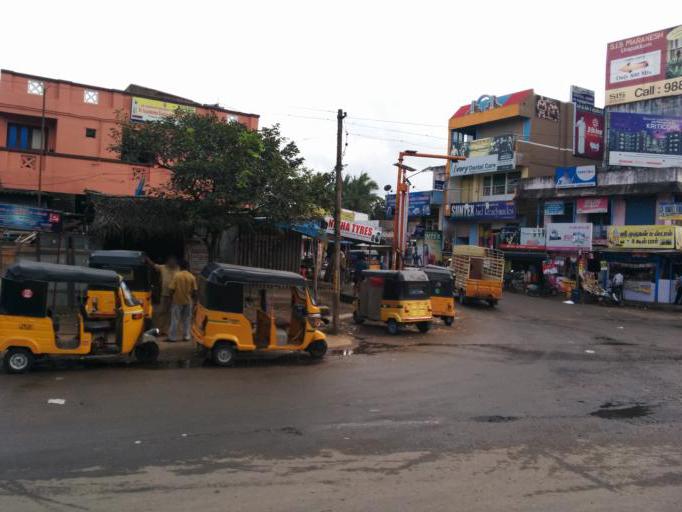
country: IN
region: Tamil Nadu
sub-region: Kancheepuram
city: Guduvancheri
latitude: 12.8602
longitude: 80.0725
